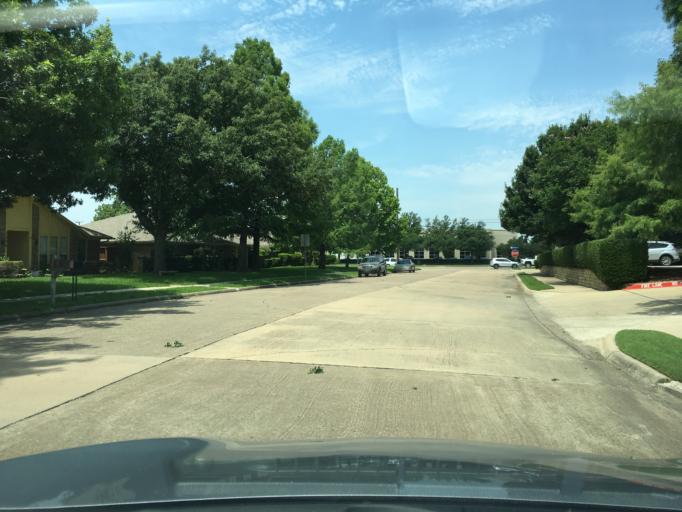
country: US
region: Texas
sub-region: Dallas County
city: Richardson
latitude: 32.9660
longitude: -96.6987
